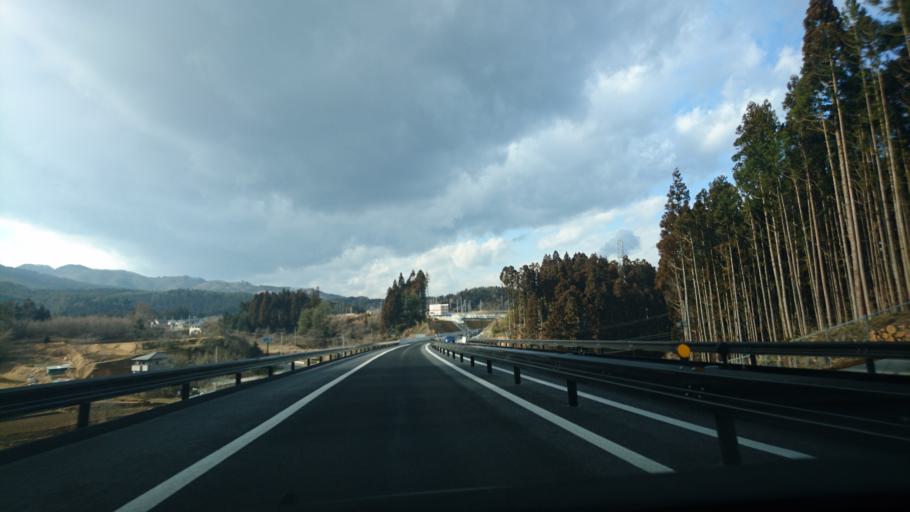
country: JP
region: Miyagi
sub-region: Oshika Gun
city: Onagawa Cho
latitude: 38.7604
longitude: 141.5013
